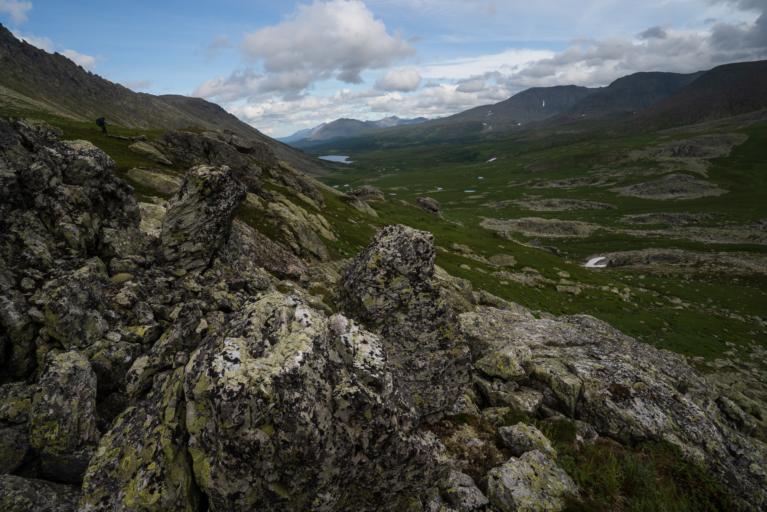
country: RU
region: Komi Republic
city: Synya
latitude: 64.7868
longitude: 59.0956
